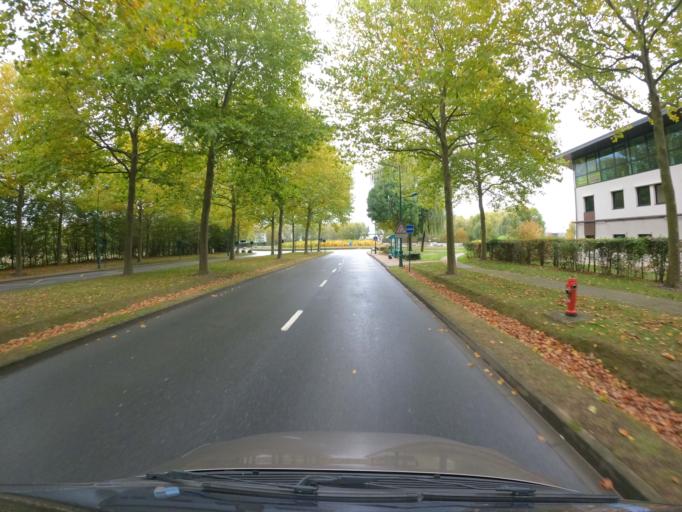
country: FR
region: Ile-de-France
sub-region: Departement de Seine-et-Marne
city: Serris
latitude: 48.8373
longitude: 2.7940
